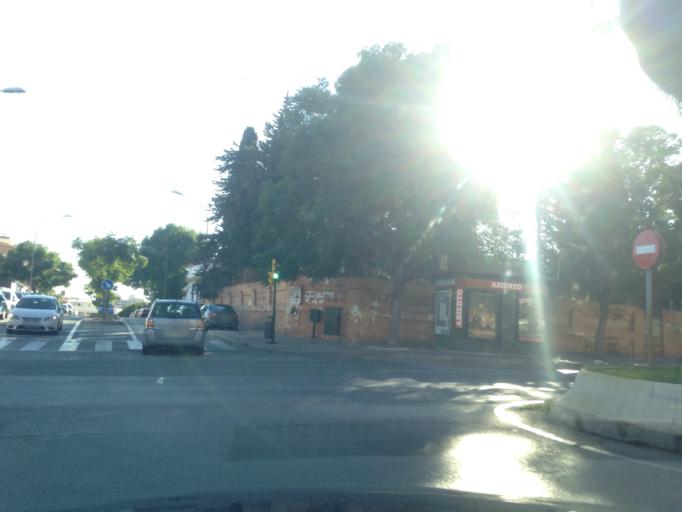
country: ES
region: Andalusia
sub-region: Provincia de Malaga
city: Malaga
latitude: 36.7247
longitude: -4.4564
